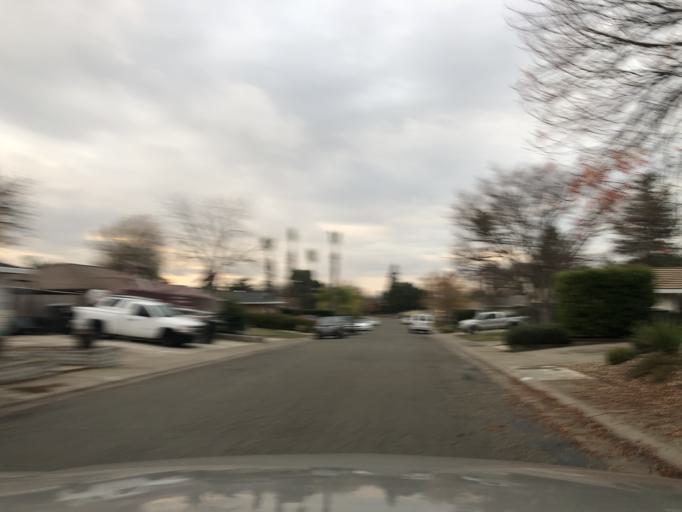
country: US
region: California
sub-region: Sacramento County
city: Foothill Farms
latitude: 38.6620
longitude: -121.3162
